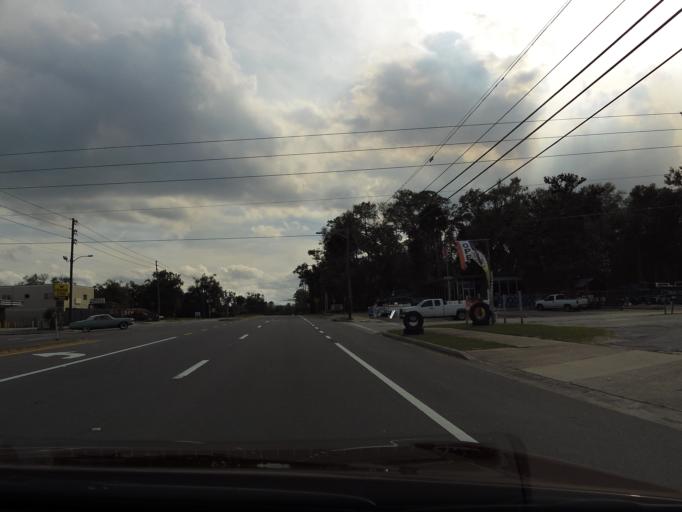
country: US
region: Florida
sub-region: Volusia County
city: De Leon Springs
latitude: 29.1200
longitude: -81.3519
